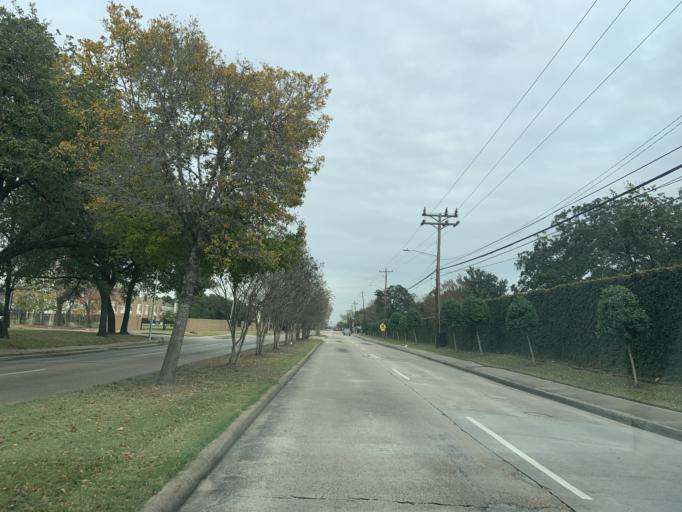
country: US
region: Texas
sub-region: Fort Bend County
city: Missouri City
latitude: 29.6810
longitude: -95.5201
